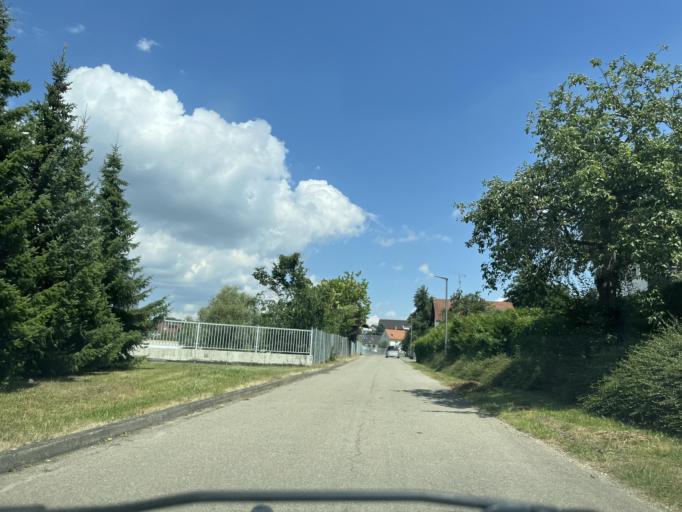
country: DE
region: Baden-Wuerttemberg
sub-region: Tuebingen Region
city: Krauchenwies
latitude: 48.0142
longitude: 9.2464
